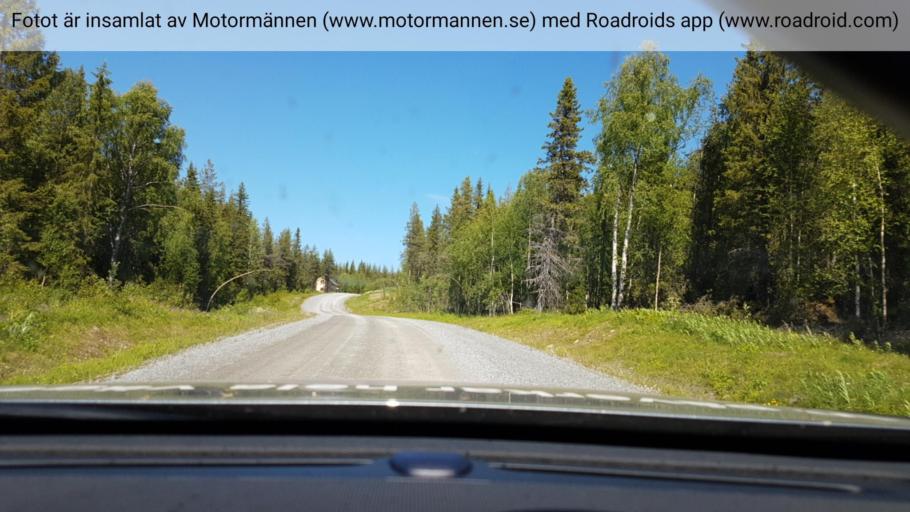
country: SE
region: Vaesterbotten
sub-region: Vilhelmina Kommun
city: Sjoberg
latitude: 64.6624
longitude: 15.7569
